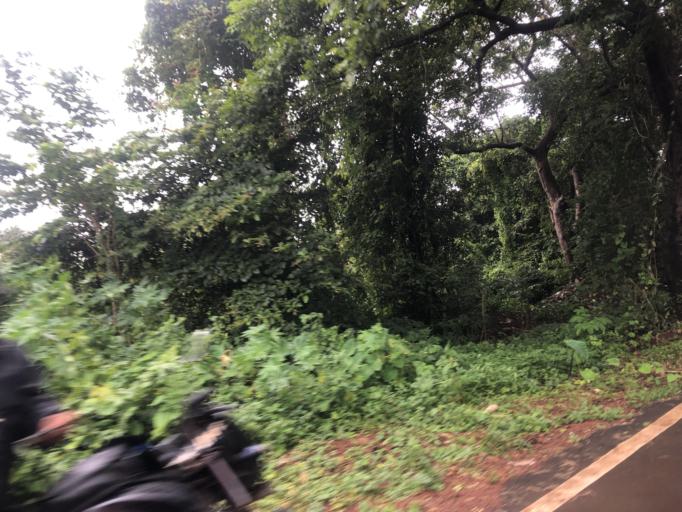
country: IN
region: Goa
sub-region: North Goa
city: Serula
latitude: 15.5396
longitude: 73.8316
